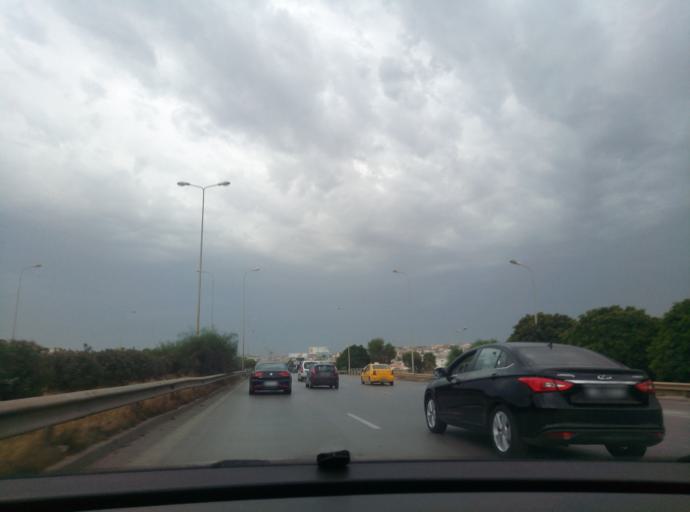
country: TN
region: Bin 'Arus
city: Ben Arous
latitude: 36.7612
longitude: 10.1985
